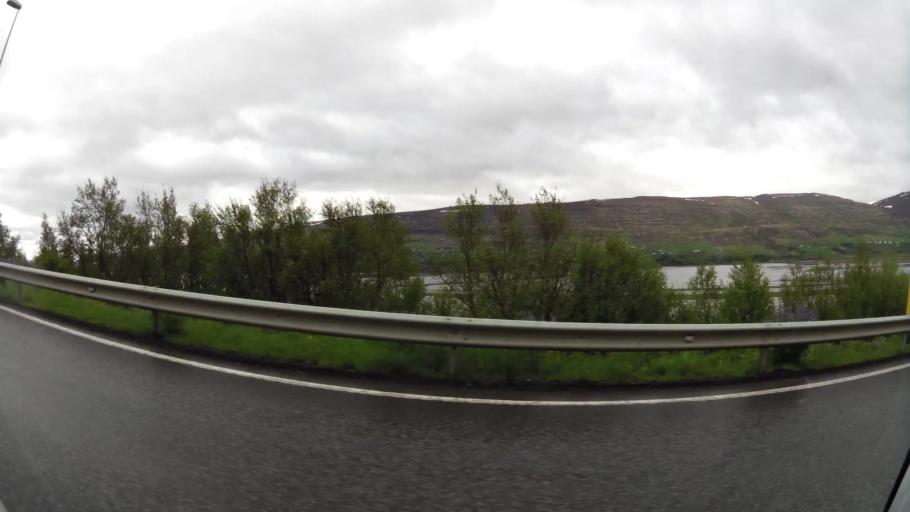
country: IS
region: Northeast
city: Akureyri
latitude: 65.6638
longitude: -18.0868
